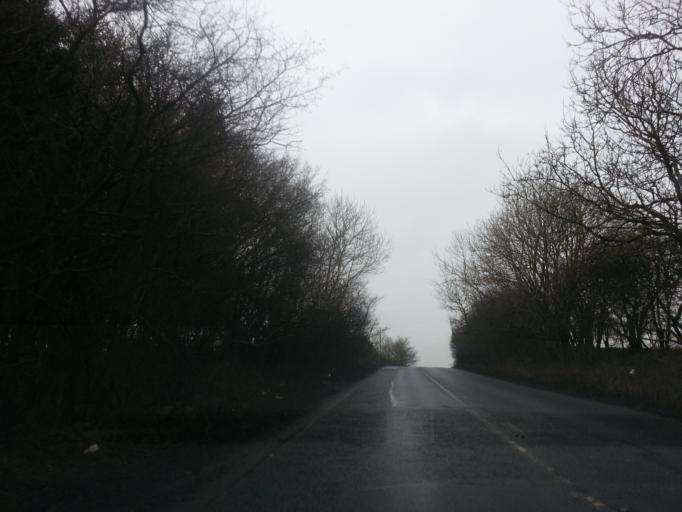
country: GB
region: England
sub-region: Darlington
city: Denton
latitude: 54.6018
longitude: -1.6738
